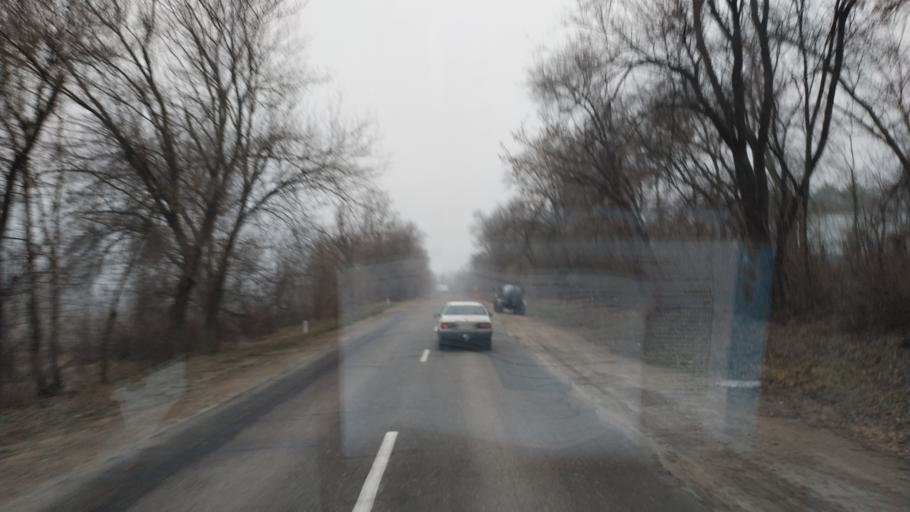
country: MD
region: Laloveni
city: Ialoveni
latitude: 46.9548
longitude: 28.7545
